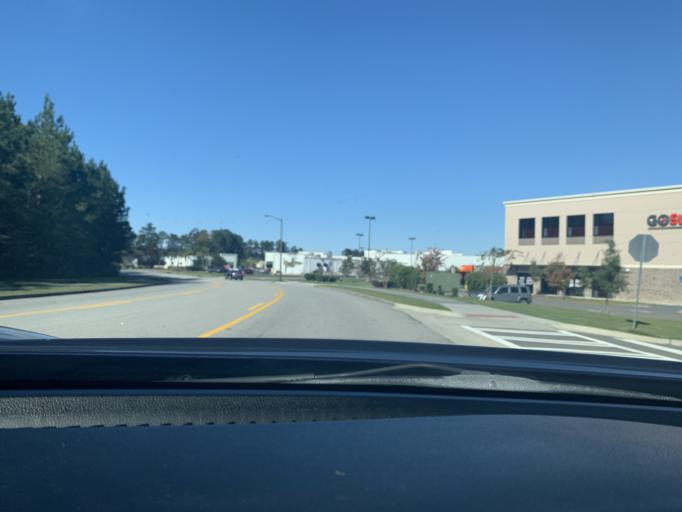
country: US
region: Georgia
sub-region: Chatham County
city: Pooler
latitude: 32.1334
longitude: -81.2507
